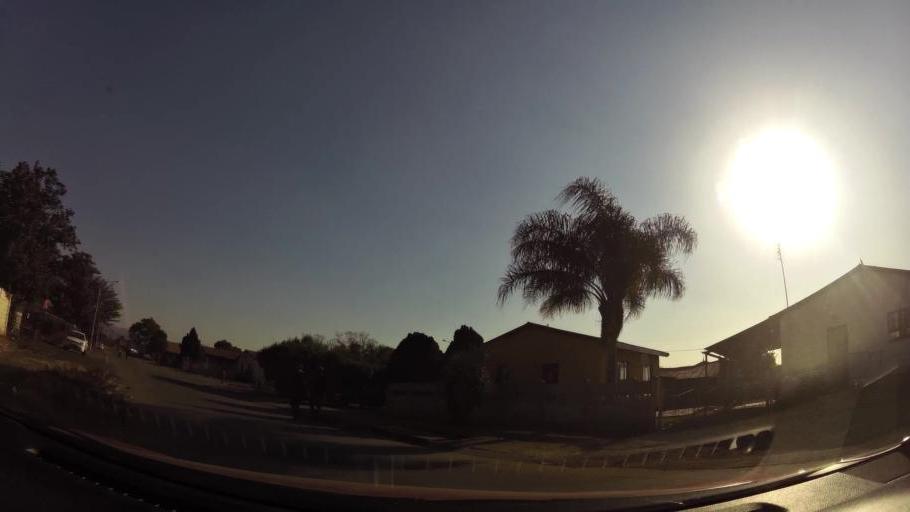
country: ZA
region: North-West
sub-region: Bojanala Platinum District Municipality
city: Rustenburg
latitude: -25.6409
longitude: 27.2380
